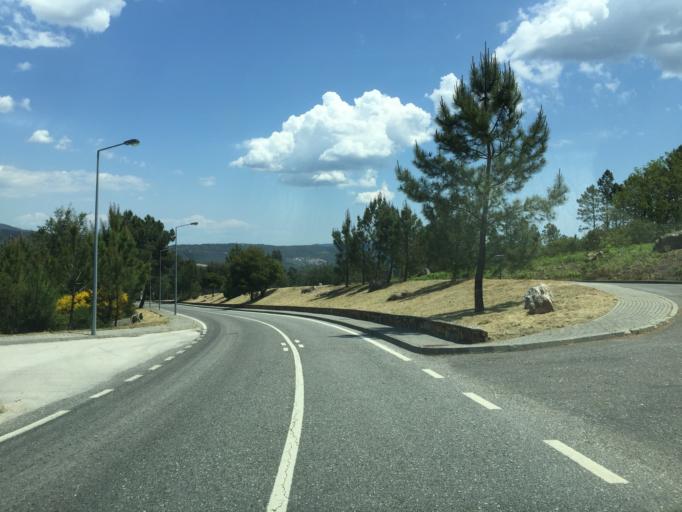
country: PT
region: Coimbra
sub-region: Pampilhosa da Serra
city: Pampilhosa da Serra
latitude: 40.0879
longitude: -7.8524
